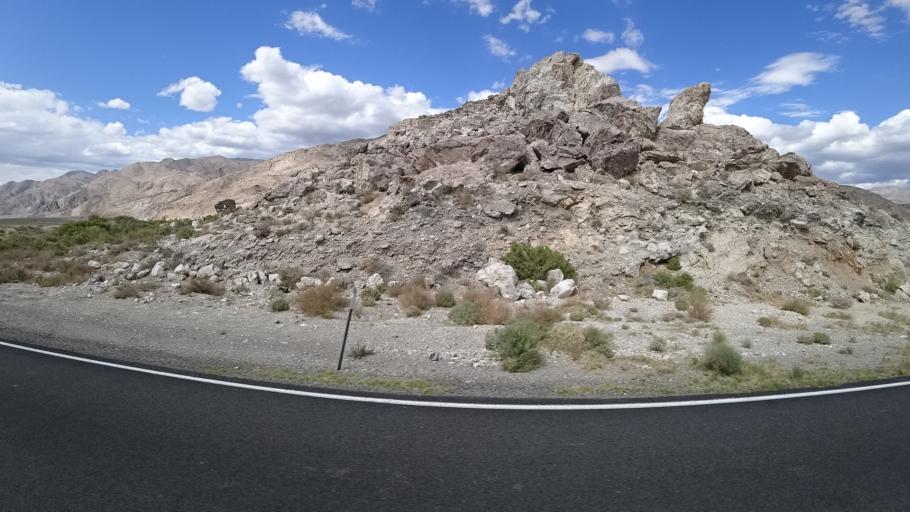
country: US
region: California
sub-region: Inyo County
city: Lone Pine
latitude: 36.5355
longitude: -117.9243
